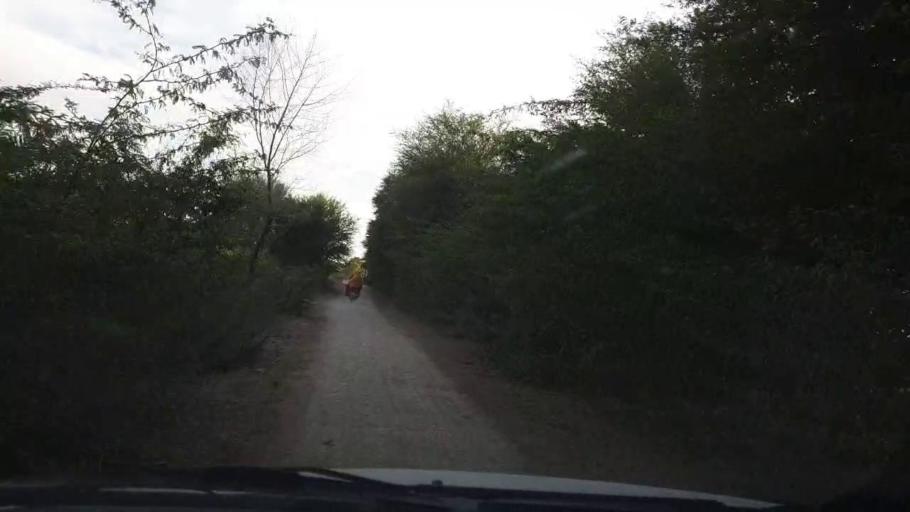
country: PK
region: Sindh
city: Pithoro
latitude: 25.6418
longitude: 69.2918
